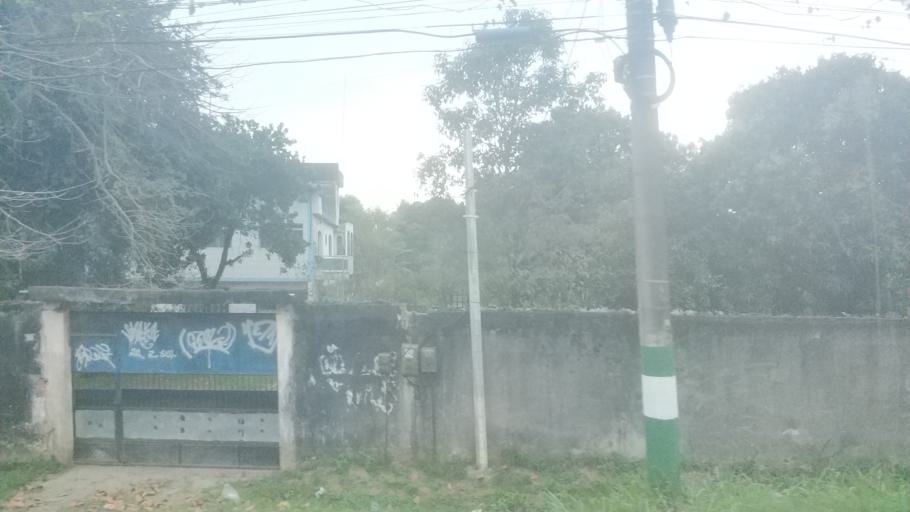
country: BR
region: Rio de Janeiro
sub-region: Seropedica
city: Seropedica
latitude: -22.8090
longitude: -43.6333
